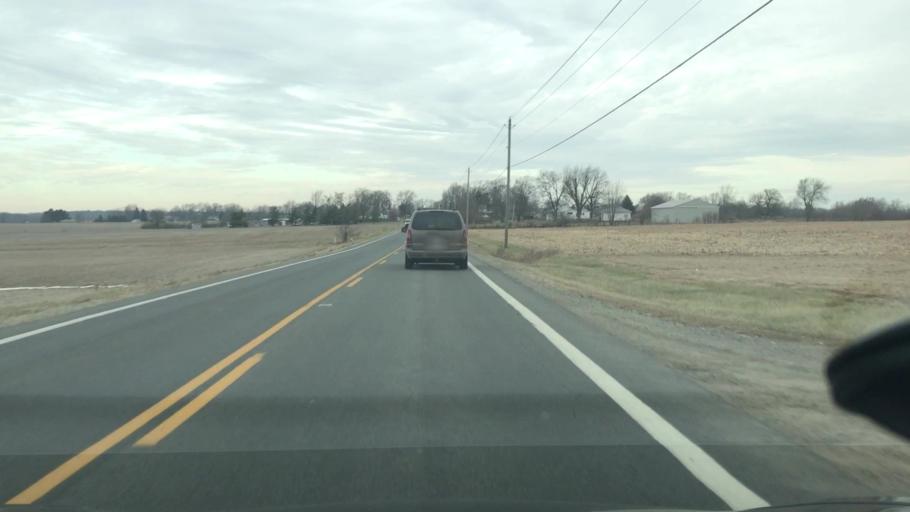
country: US
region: Ohio
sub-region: Madison County
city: Choctaw Lake
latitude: 39.9269
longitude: -83.4880
